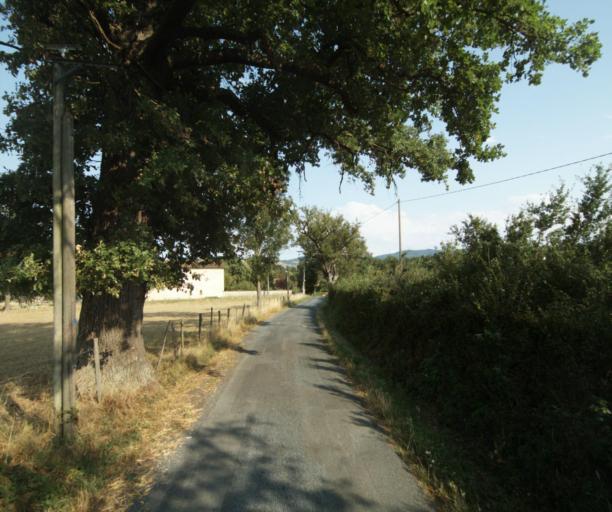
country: FR
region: Rhone-Alpes
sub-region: Departement du Rhone
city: Savigny
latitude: 45.8253
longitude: 4.5838
